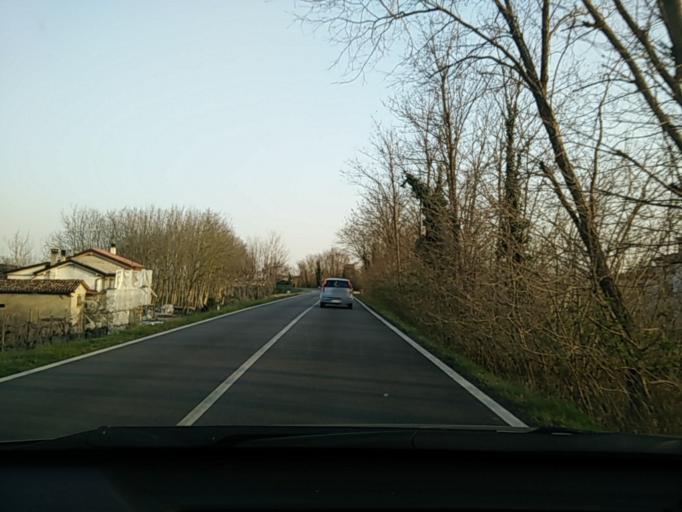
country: IT
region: Veneto
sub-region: Provincia di Treviso
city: Zenson di Piave
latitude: 45.6638
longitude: 12.5002
